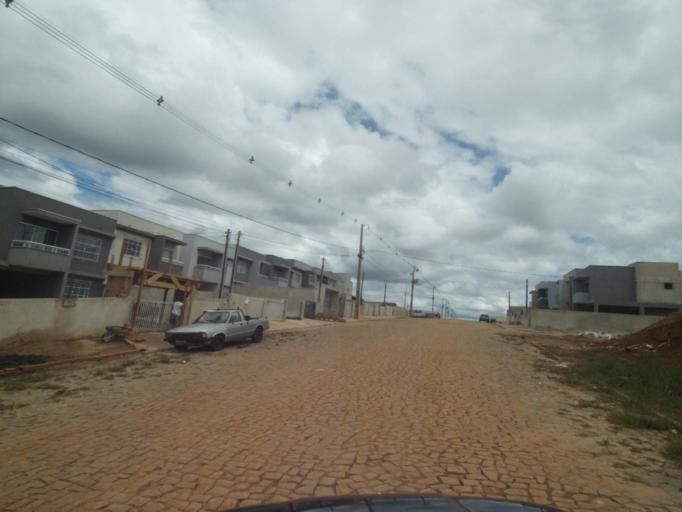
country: BR
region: Parana
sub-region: Telemaco Borba
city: Telemaco Borba
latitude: -24.3058
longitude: -50.6364
